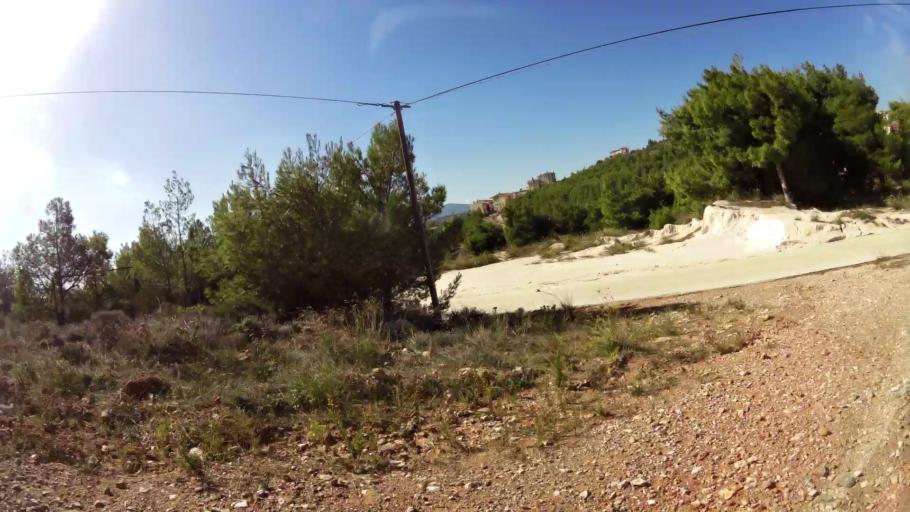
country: GR
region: Attica
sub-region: Nomarchia Anatolikis Attikis
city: Dioni
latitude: 38.0301
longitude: 23.9334
